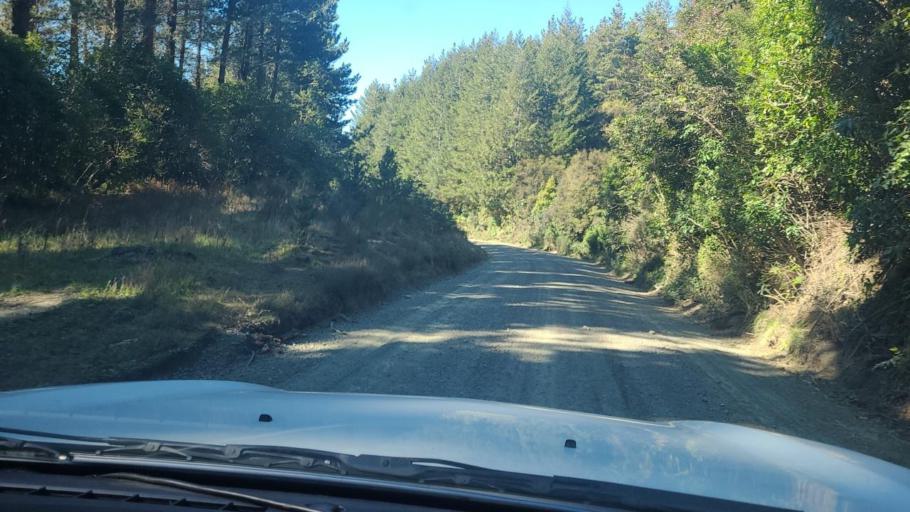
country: NZ
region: Hawke's Bay
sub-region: Napier City
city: Taradale
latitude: -39.4078
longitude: 176.4656
